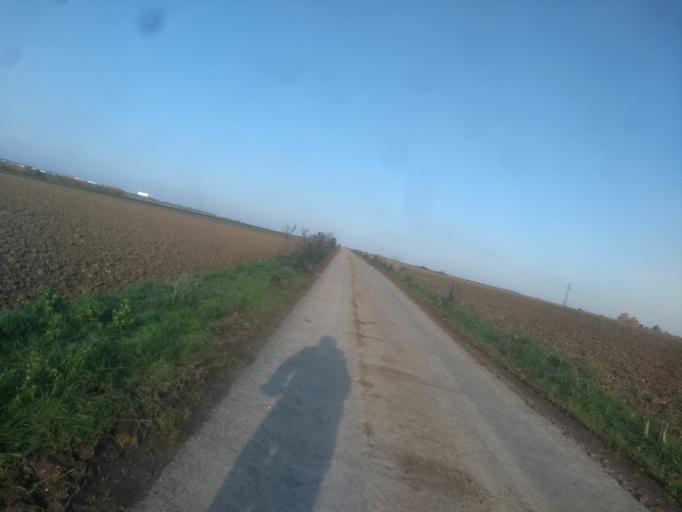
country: FR
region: Nord-Pas-de-Calais
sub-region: Departement du Pas-de-Calais
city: Tilloy-les-Mofflaines
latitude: 50.2812
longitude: 2.8218
